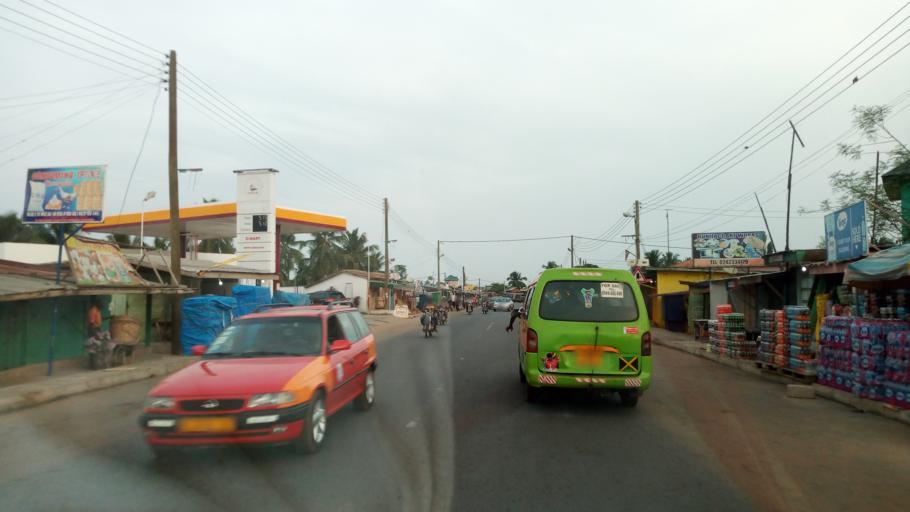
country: TG
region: Maritime
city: Lome
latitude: 6.1190
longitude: 1.1885
